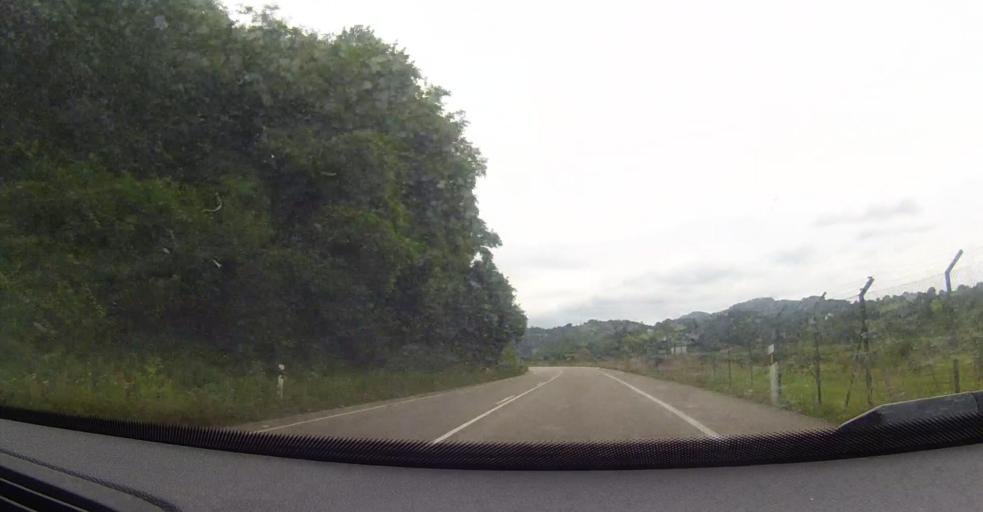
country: ES
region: Asturias
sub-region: Province of Asturias
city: Pilona
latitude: 43.3666
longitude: -5.2920
